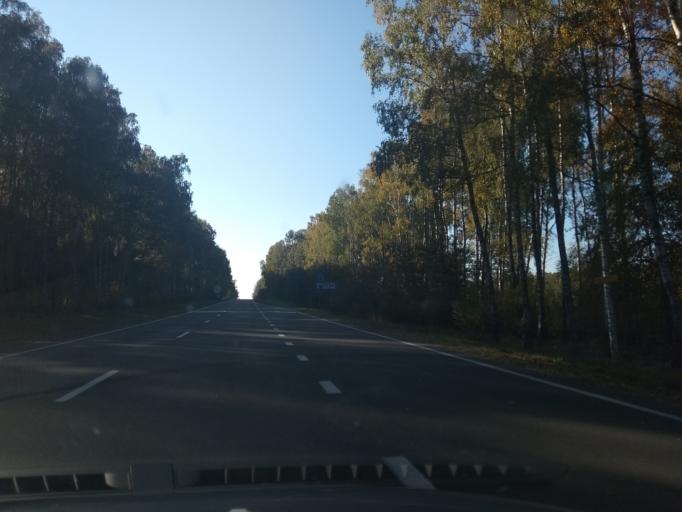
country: BY
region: Grodnenskaya
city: Vyalikaya Byerastavitsa
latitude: 53.1177
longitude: 24.0164
